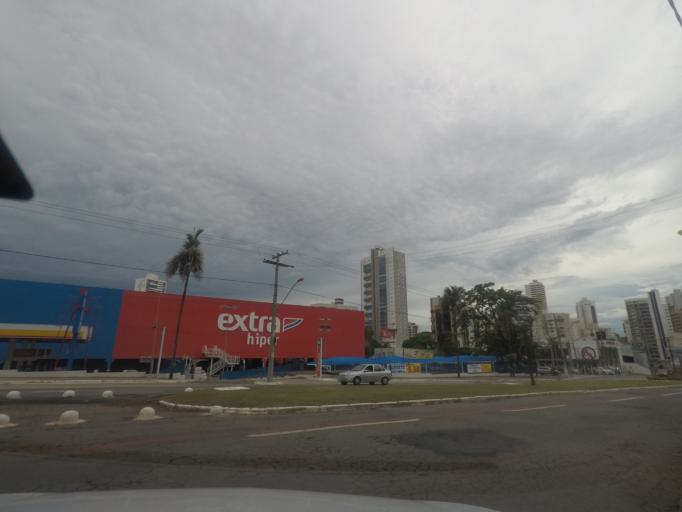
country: BR
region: Goias
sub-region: Goiania
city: Goiania
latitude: -16.6925
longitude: -49.2697
